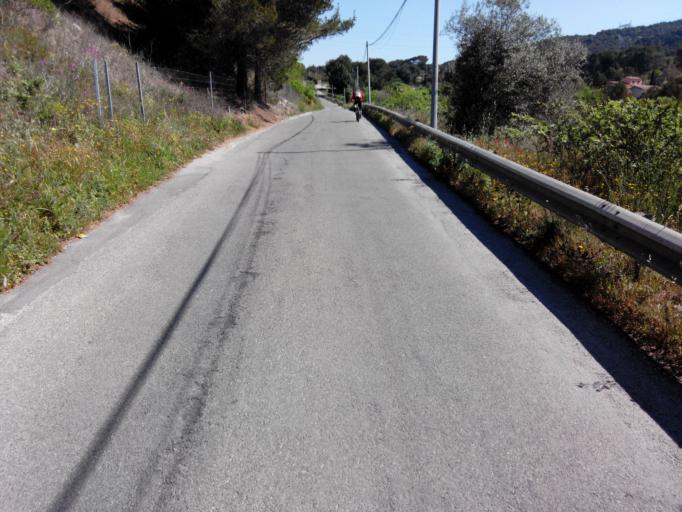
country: FR
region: Provence-Alpes-Cote d'Azur
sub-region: Departement des Bouches-du-Rhone
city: Roquevaire
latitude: 43.3470
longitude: 5.6162
